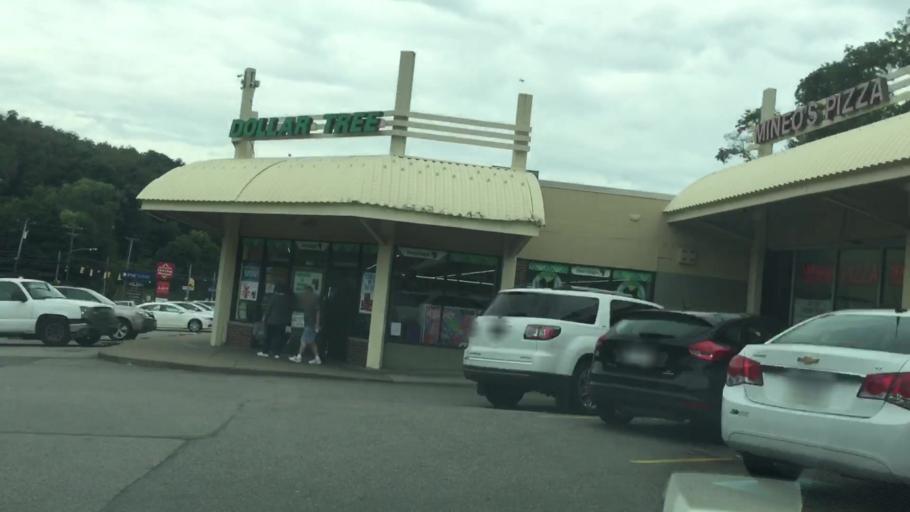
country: US
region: Pennsylvania
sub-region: Allegheny County
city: Crafton
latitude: 40.4275
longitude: -80.0554
